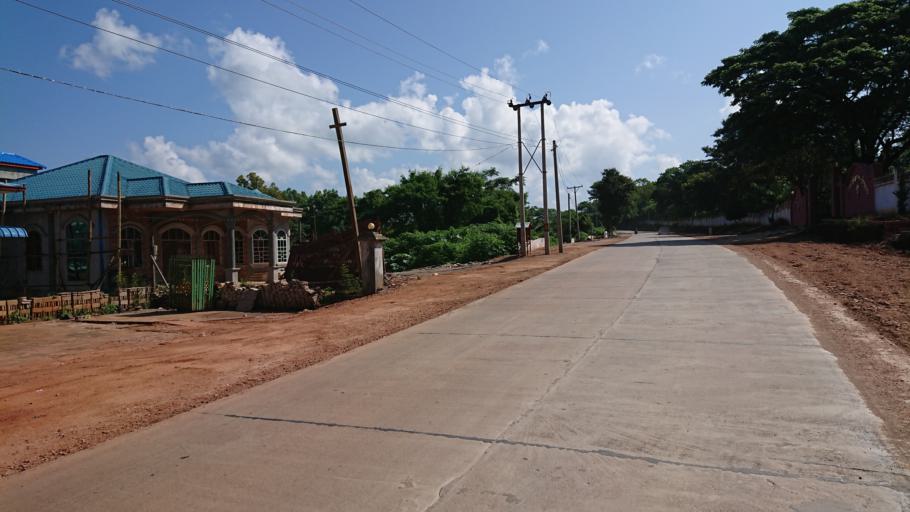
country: MM
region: Shan
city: Taunggyi
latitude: 20.8019
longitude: 97.1827
